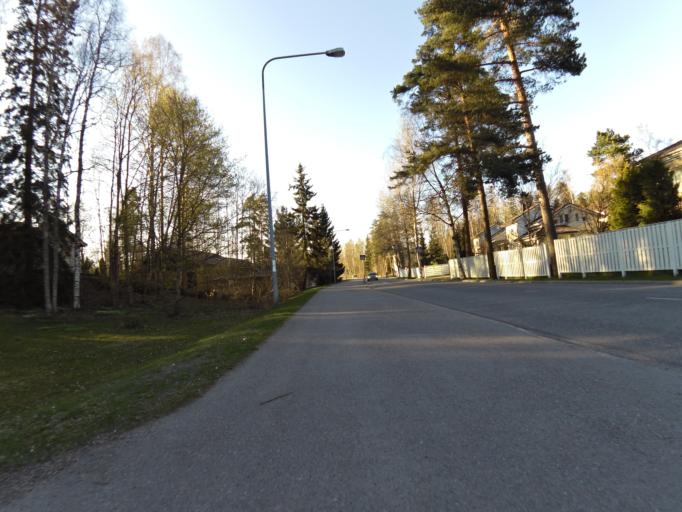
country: FI
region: Uusimaa
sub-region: Helsinki
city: Espoo
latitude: 60.1587
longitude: 24.6804
